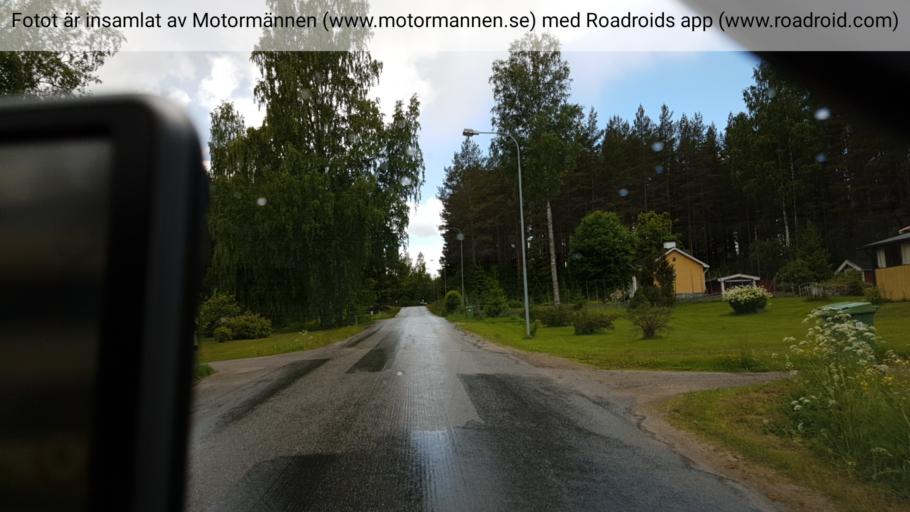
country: SE
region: Gaevleborg
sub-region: Bollnas Kommun
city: Arbra
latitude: 61.4625
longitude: 16.3652
